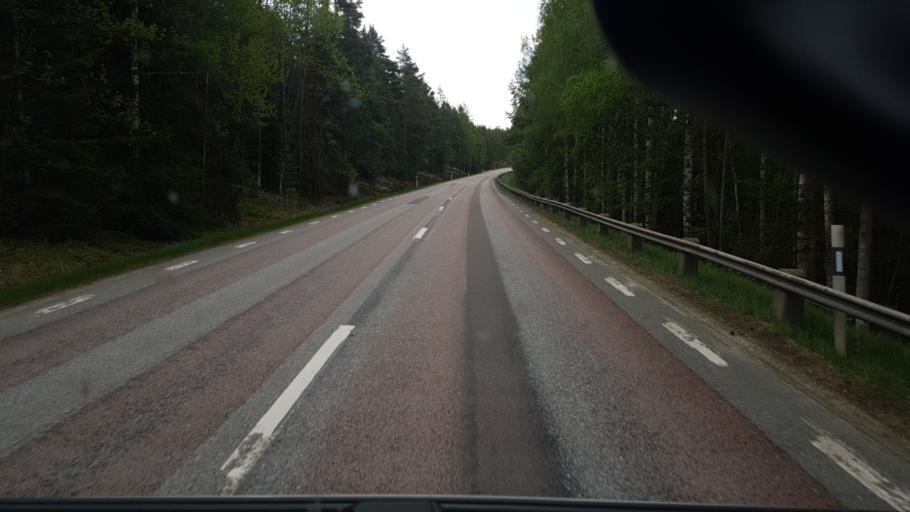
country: SE
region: Vaermland
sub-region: Arvika Kommun
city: Arvika
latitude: 59.5651
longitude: 12.7206
